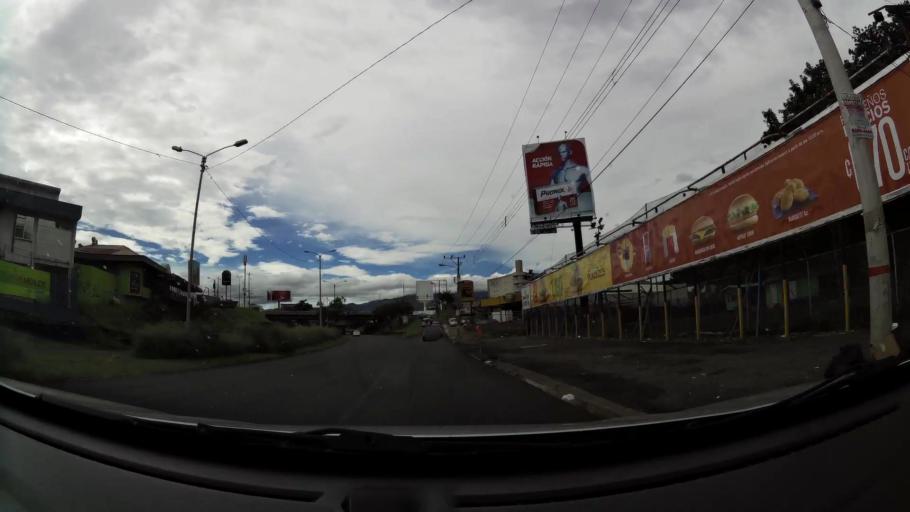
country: CR
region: San Jose
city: San Pedro
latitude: 9.9260
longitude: -84.0559
